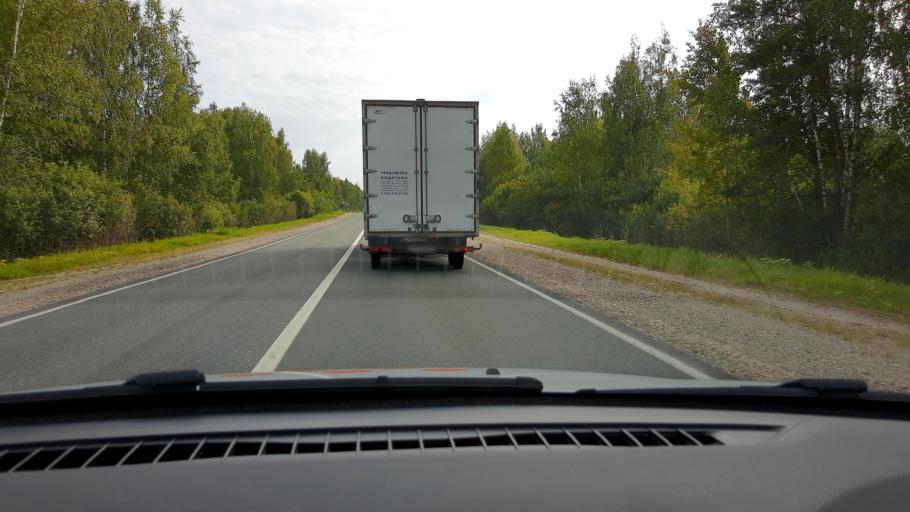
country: RU
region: Nizjnij Novgorod
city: Sukhobezvodnoye
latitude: 56.8423
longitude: 44.7429
